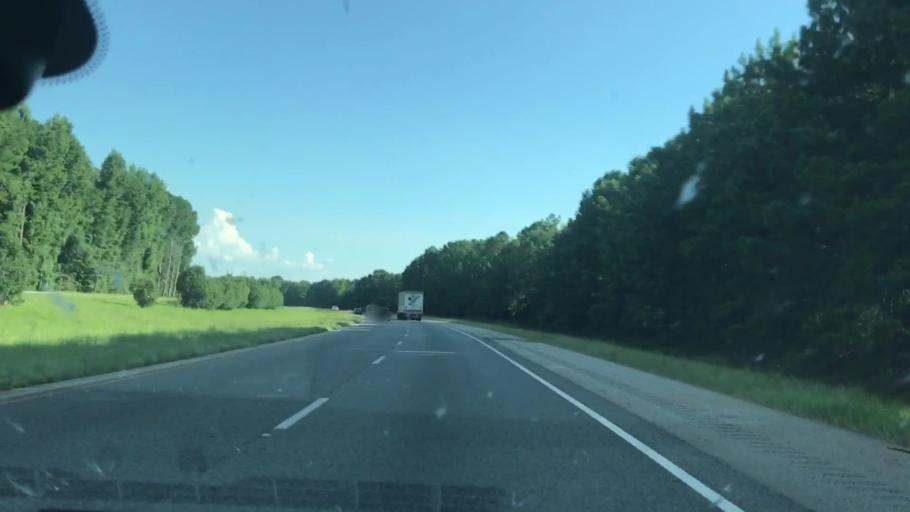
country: US
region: Georgia
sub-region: Troup County
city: La Grange
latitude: 32.9449
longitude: -84.9573
